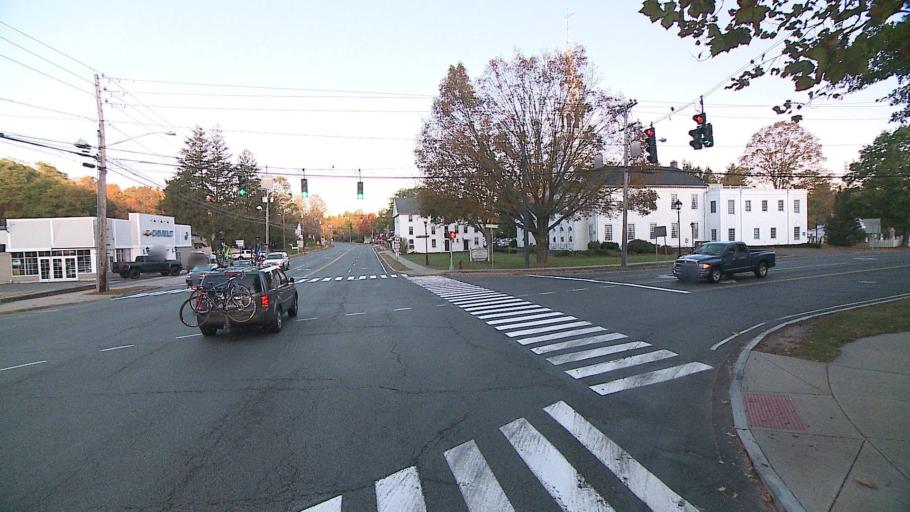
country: US
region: Connecticut
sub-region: Hartford County
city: Weatogue
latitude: 41.8096
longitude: -72.8304
